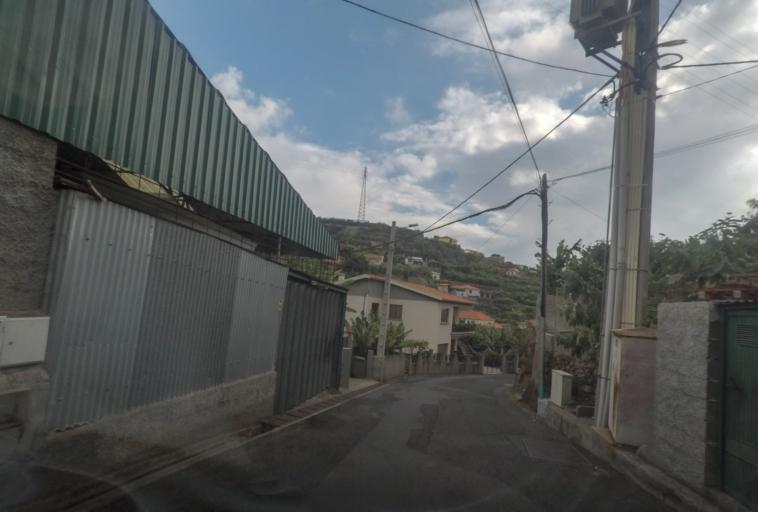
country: PT
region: Madeira
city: Camara de Lobos
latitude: 32.6546
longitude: -16.9587
